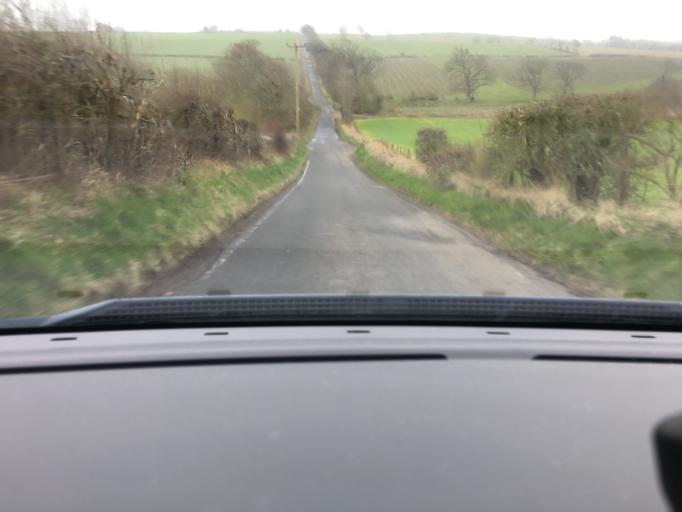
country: GB
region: Scotland
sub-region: West Lothian
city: Linlithgow
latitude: 55.9654
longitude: -3.5552
